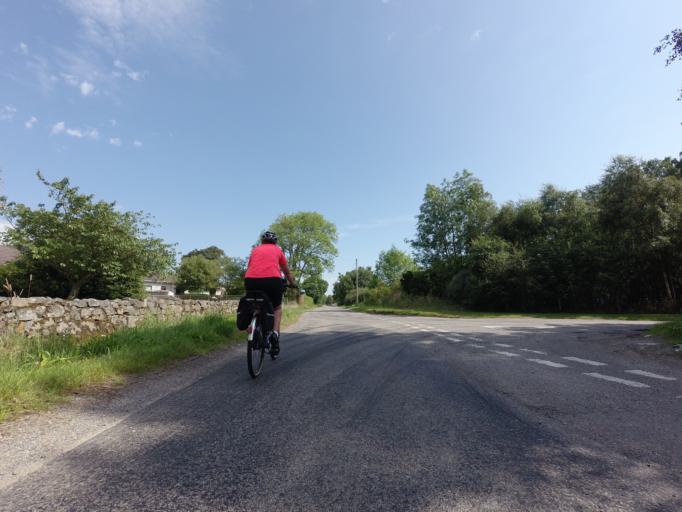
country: GB
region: Scotland
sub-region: Highland
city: Invergordon
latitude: 57.7275
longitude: -4.1953
